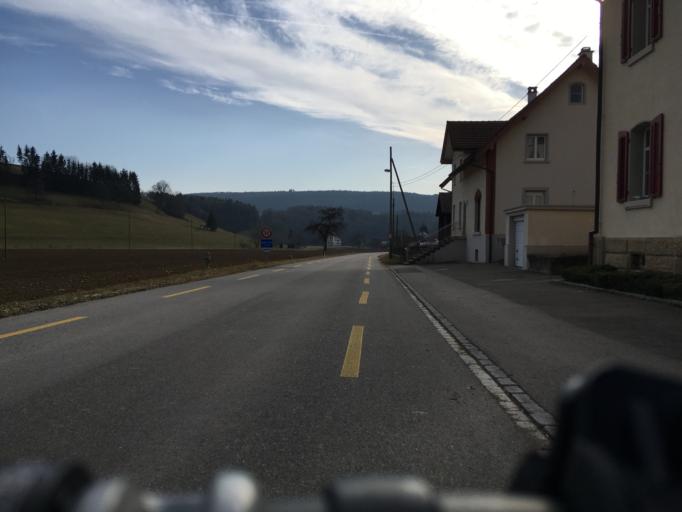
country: DE
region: Baden-Wuerttemberg
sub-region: Freiburg Region
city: Tengen
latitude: 47.7864
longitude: 8.6808
